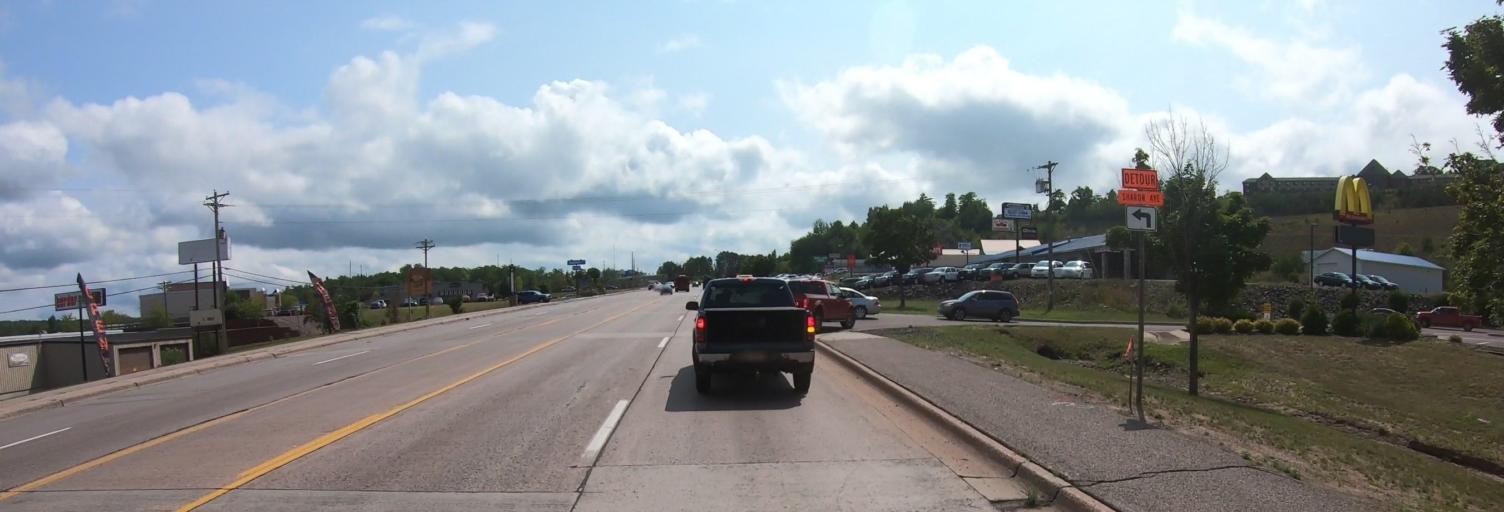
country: US
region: Michigan
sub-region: Houghton County
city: Hancock
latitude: 47.1105
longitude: -88.5898
